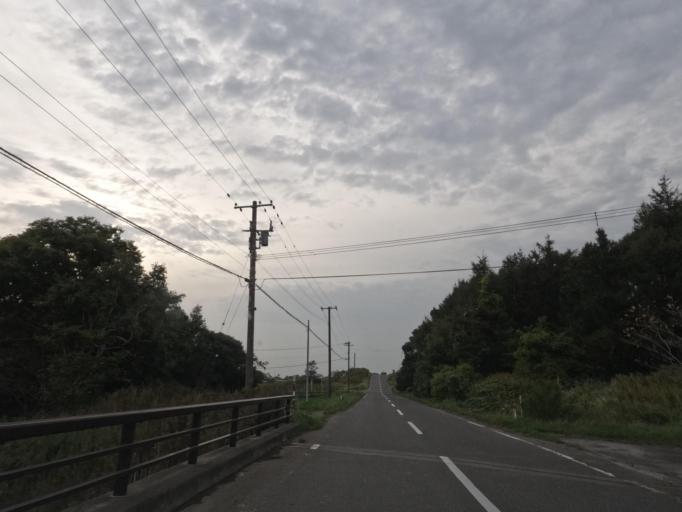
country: JP
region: Hokkaido
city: Date
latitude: 42.4174
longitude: 140.9215
